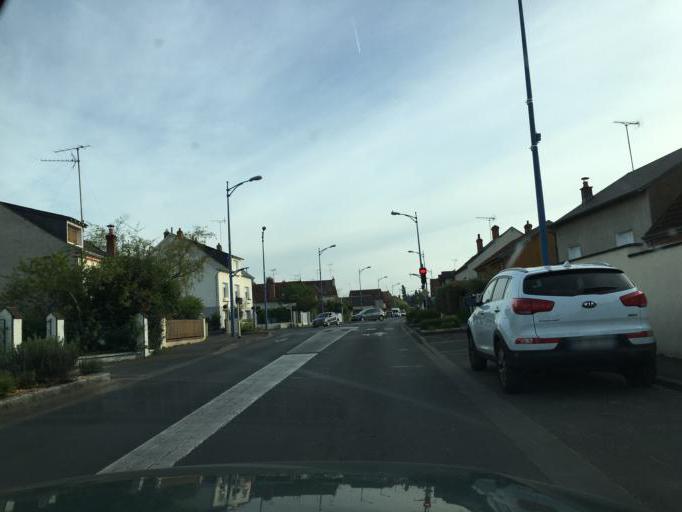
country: FR
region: Centre
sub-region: Departement du Loiret
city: Fleury-les-Aubrais
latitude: 47.9269
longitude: 1.9159
